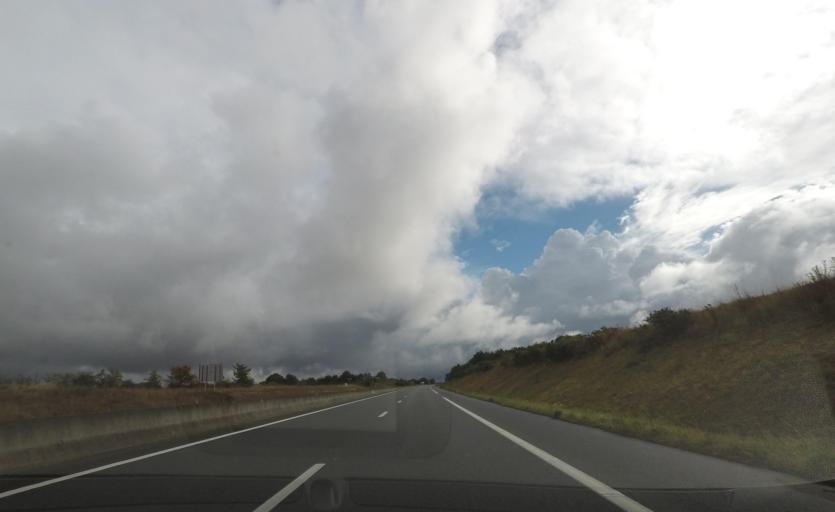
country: FR
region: Pays de la Loire
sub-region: Departement de la Vendee
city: La Roche-sur-Yon
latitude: 46.6531
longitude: -1.3845
